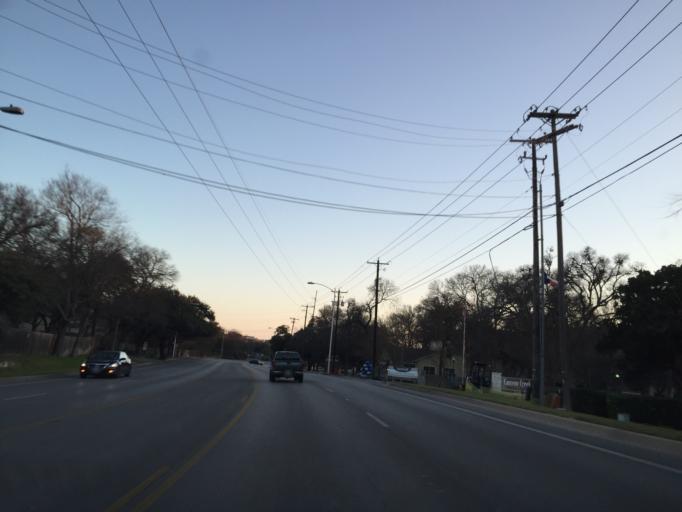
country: US
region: Texas
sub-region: Williamson County
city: Jollyville
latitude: 30.4116
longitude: -97.7480
